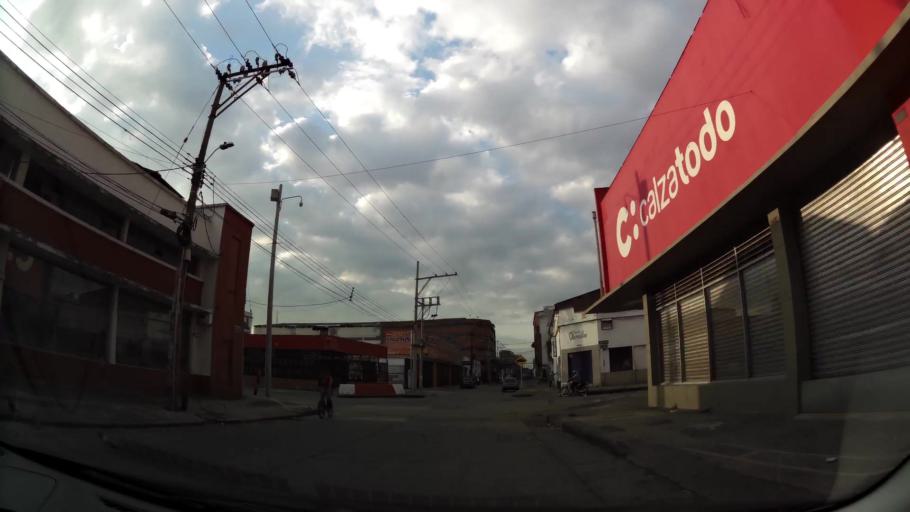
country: CO
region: Valle del Cauca
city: Cali
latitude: 3.4543
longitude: -76.5205
